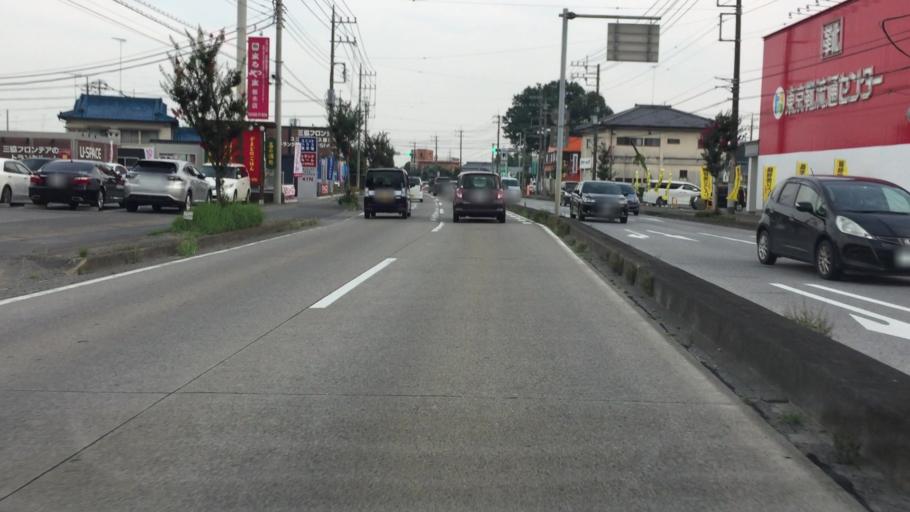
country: JP
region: Tochigi
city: Tochigi
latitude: 36.3733
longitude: 139.7154
